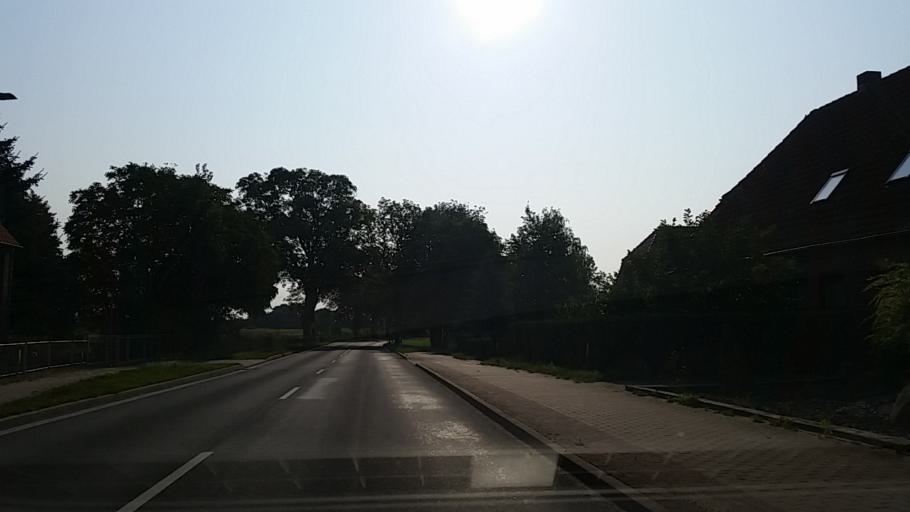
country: DE
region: Mecklenburg-Vorpommern
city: Hagenow
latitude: 53.4669
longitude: 11.1599
